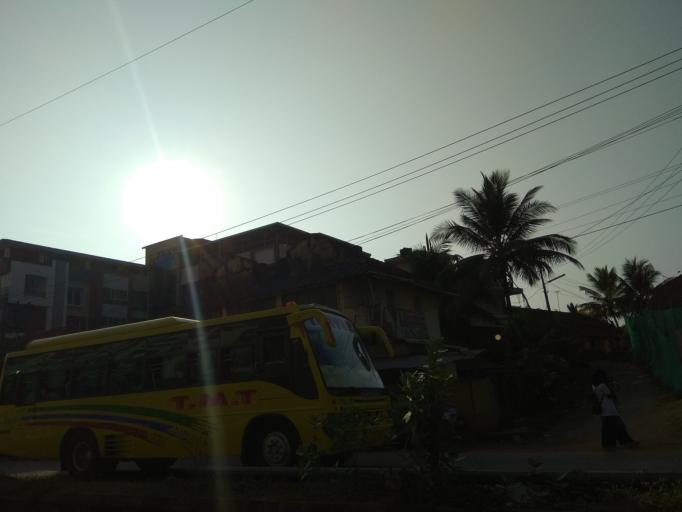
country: IN
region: Karnataka
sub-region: Dakshina Kannada
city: Mangalore
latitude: 12.9026
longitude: 74.8455
